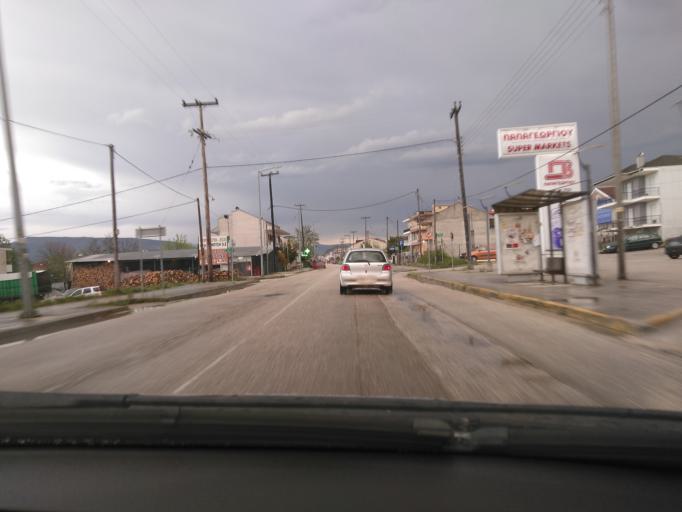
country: GR
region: Epirus
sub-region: Nomos Ioanninon
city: Anatoli
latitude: 39.6371
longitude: 20.8706
